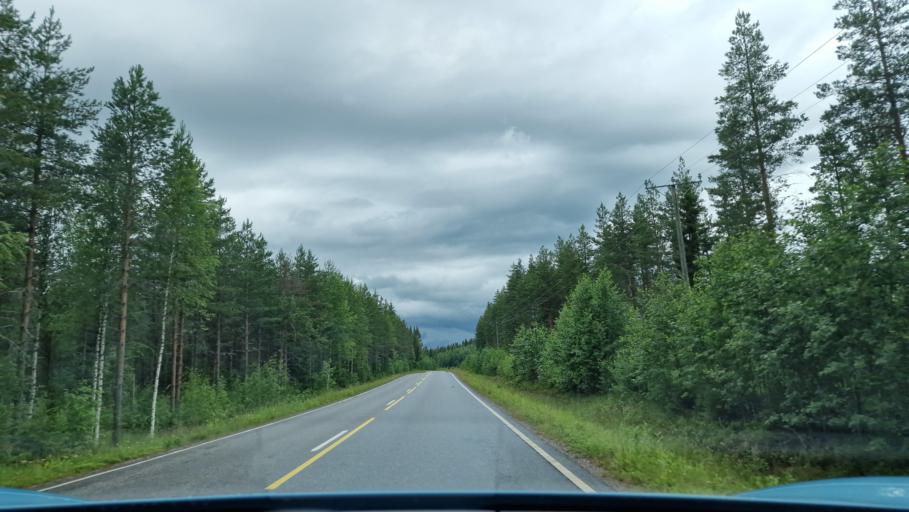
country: FI
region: Southern Ostrobothnia
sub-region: Jaerviseutu
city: Soini
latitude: 62.7232
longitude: 24.4252
